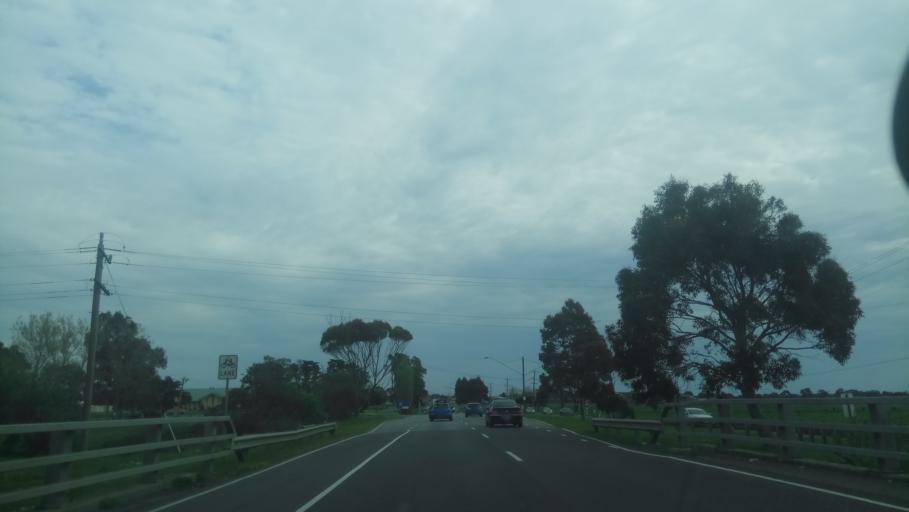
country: AU
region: Victoria
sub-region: Kingston
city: Waterways
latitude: -38.0213
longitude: 145.1374
